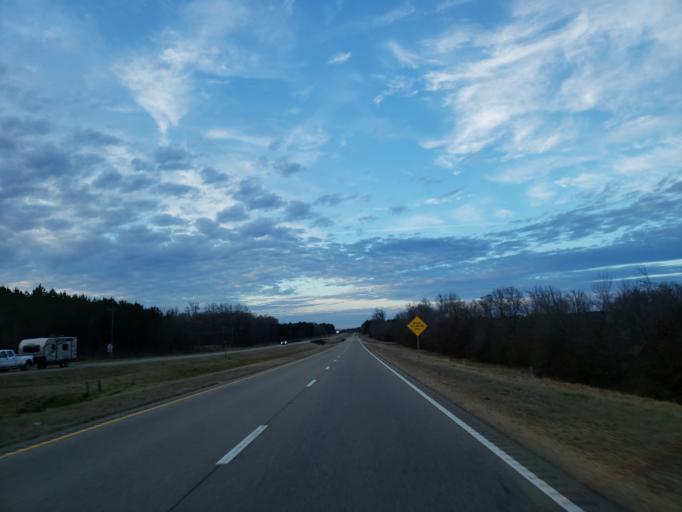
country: US
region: Mississippi
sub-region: Kemper County
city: De Kalb
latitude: 32.8141
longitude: -88.4566
